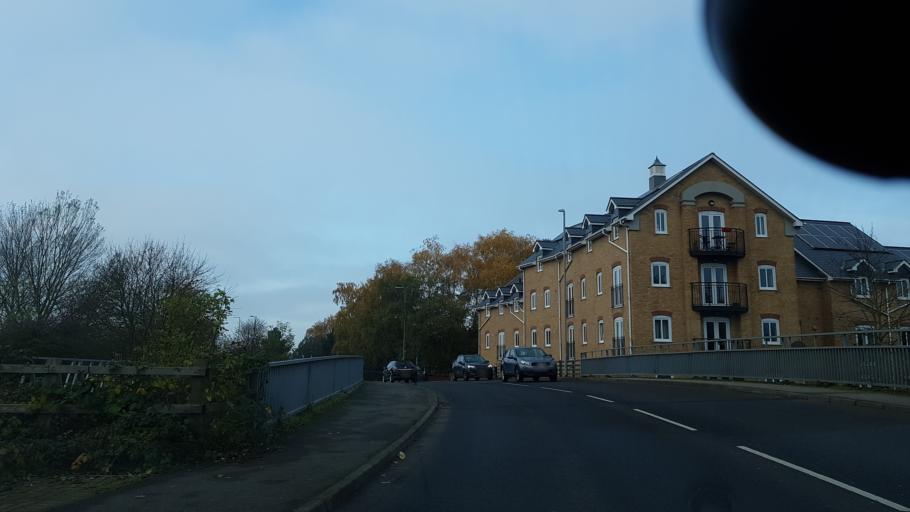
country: GB
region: England
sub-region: Central Bedfordshire
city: Biggleswade
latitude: 52.0927
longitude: -0.2688
